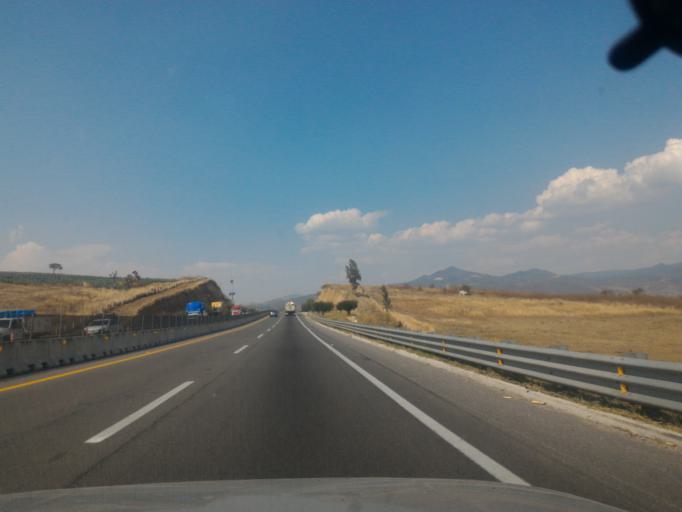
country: MX
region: Jalisco
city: Gomez Farias
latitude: 19.7988
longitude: -103.5030
